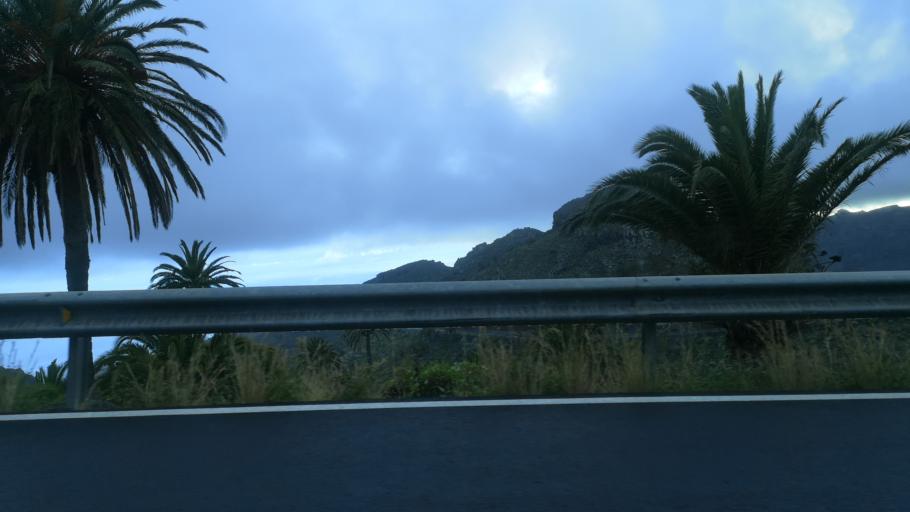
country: ES
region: Canary Islands
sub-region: Provincia de Santa Cruz de Tenerife
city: Alajero
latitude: 28.0773
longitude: -17.2071
